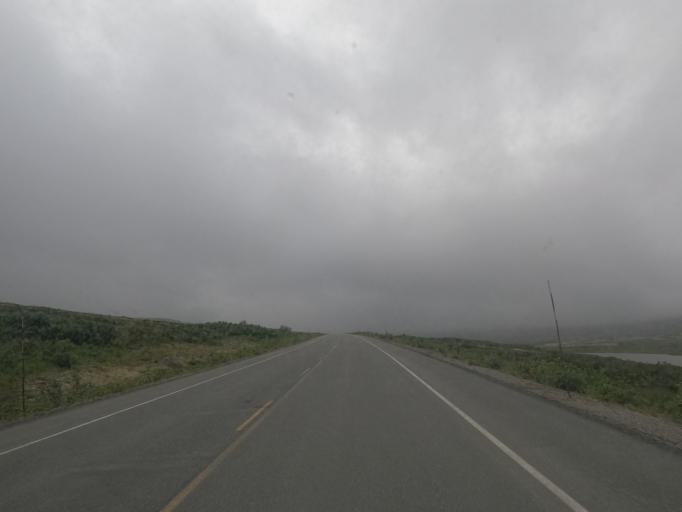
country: US
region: Alaska
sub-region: Haines Borough
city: Haines
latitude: 59.6890
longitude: -136.5830
